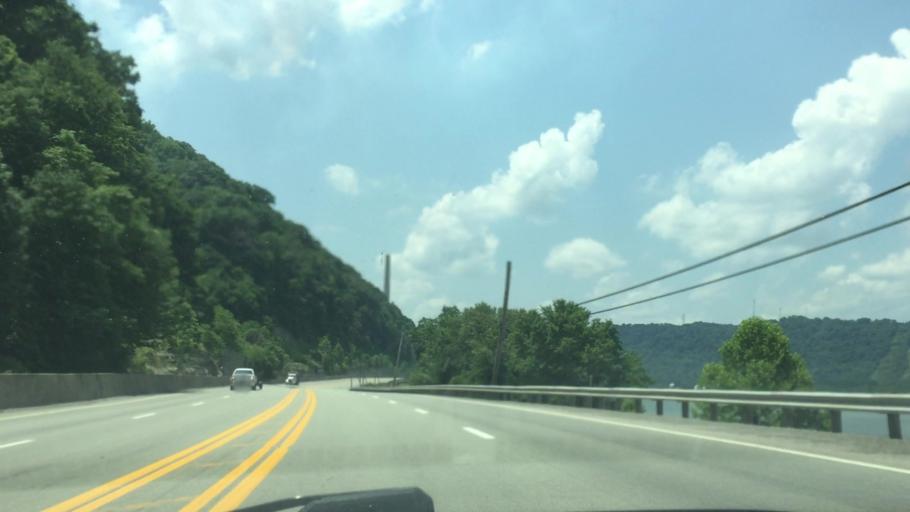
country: US
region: Ohio
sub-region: Belmont County
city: Powhatan Point
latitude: 39.8566
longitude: -80.7989
